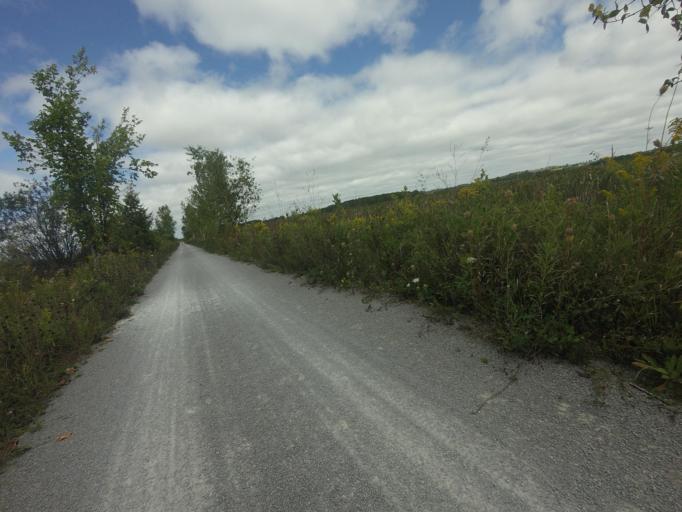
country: CA
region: Ontario
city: Uxbridge
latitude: 44.1558
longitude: -79.0818
